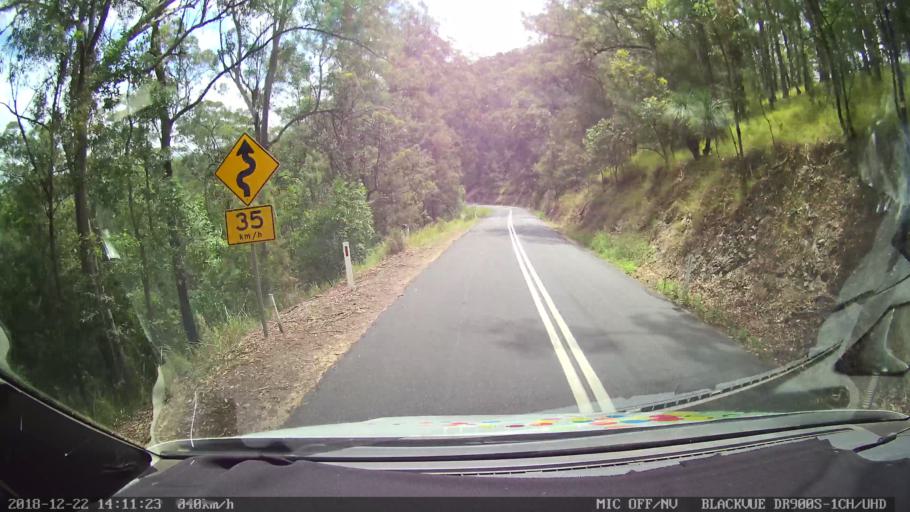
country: AU
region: New South Wales
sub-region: Clarence Valley
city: Coutts Crossing
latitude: -29.9973
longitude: 152.7103
